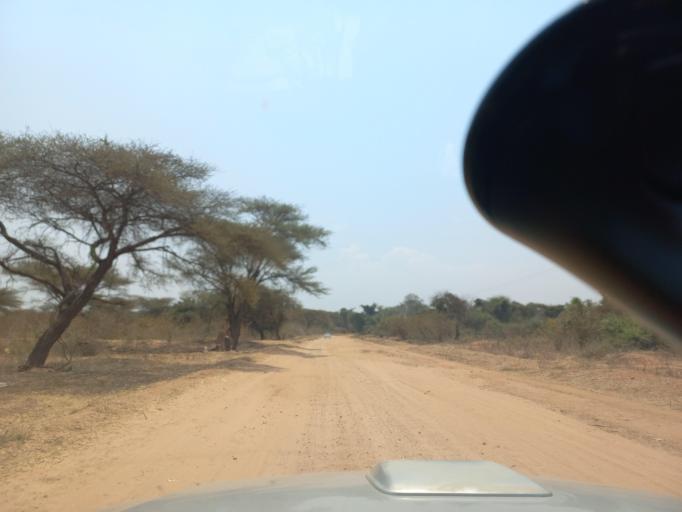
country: ZW
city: Chirundu
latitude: -15.9348
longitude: 28.8717
